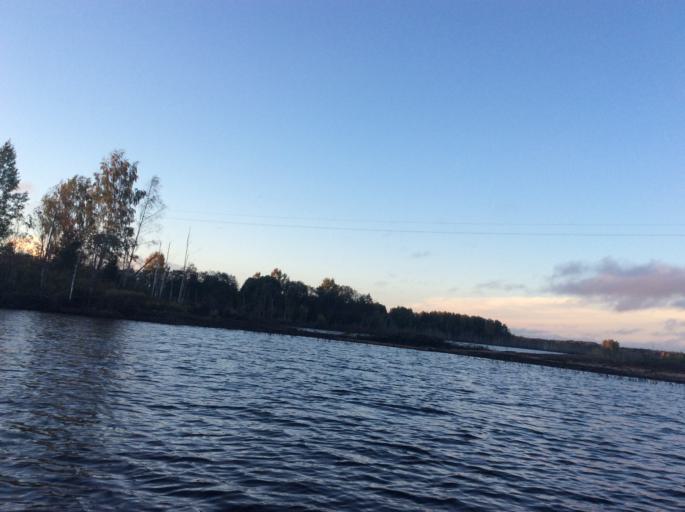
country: RU
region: Vologda
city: Ferapontovo
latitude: 59.9720
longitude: 38.6230
